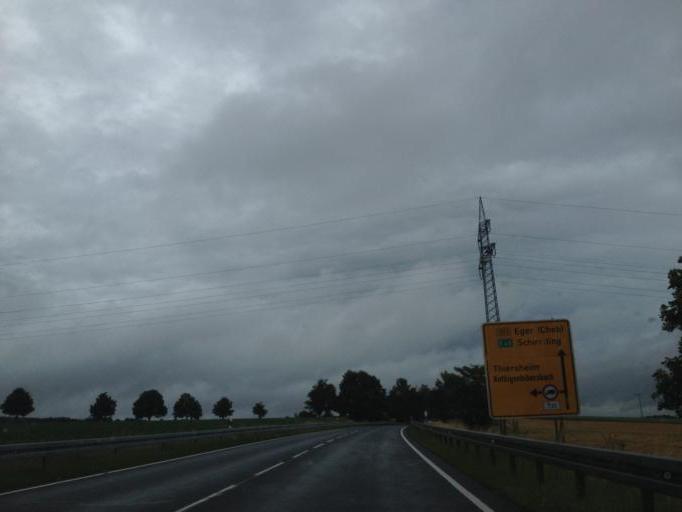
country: DE
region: Bavaria
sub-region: Upper Franconia
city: Arzberg
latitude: 50.0724
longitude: 12.1883
